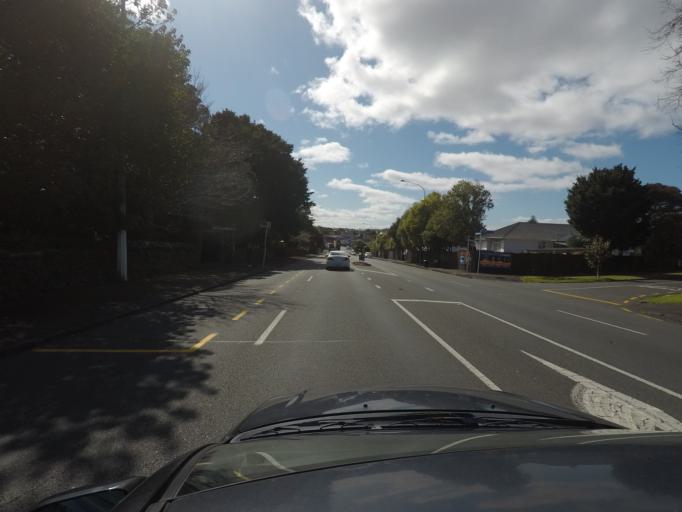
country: NZ
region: Auckland
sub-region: Auckland
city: Auckland
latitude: -36.8813
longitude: 174.7223
